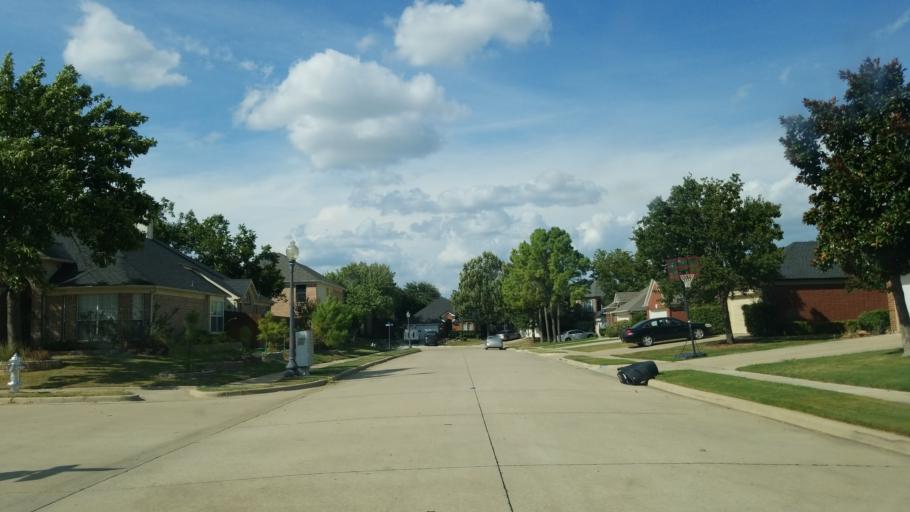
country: US
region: Texas
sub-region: Tarrant County
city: Euless
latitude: 32.8541
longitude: -97.0776
